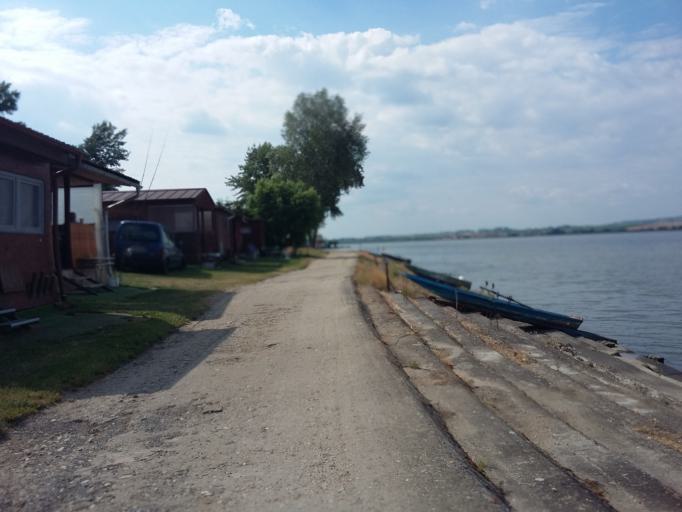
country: CZ
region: South Moravian
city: Sakvice
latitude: 48.8827
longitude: 16.6721
